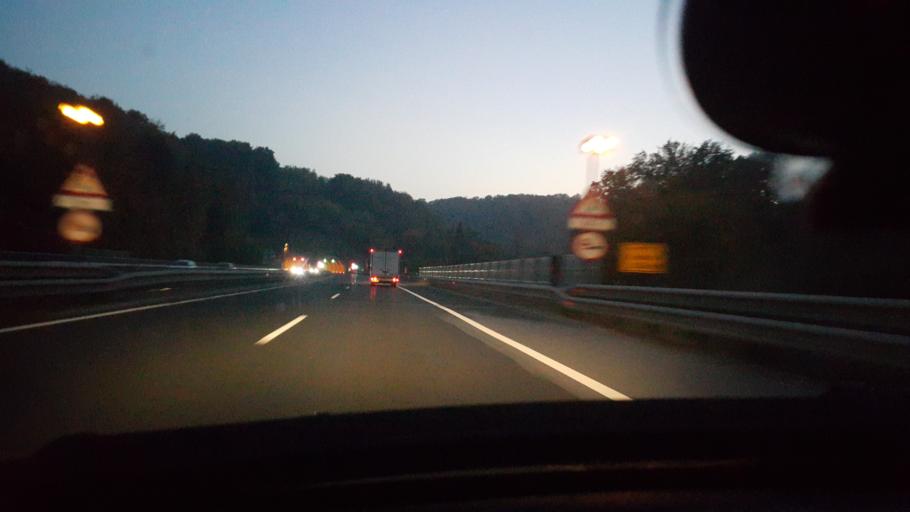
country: SI
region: Pesnica
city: Pesnica pri Mariboru
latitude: 46.5700
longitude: 15.6866
